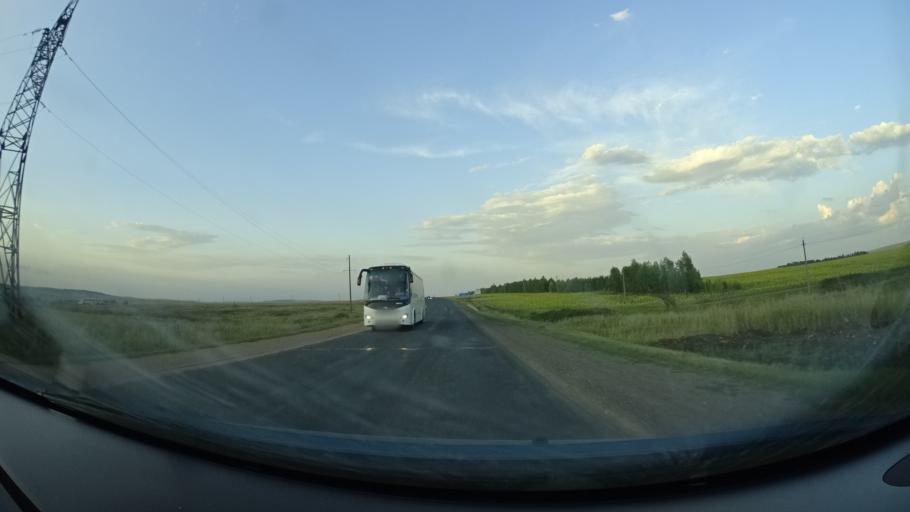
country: RU
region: Orenburg
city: Severnoye
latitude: 54.0900
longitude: 52.4542
